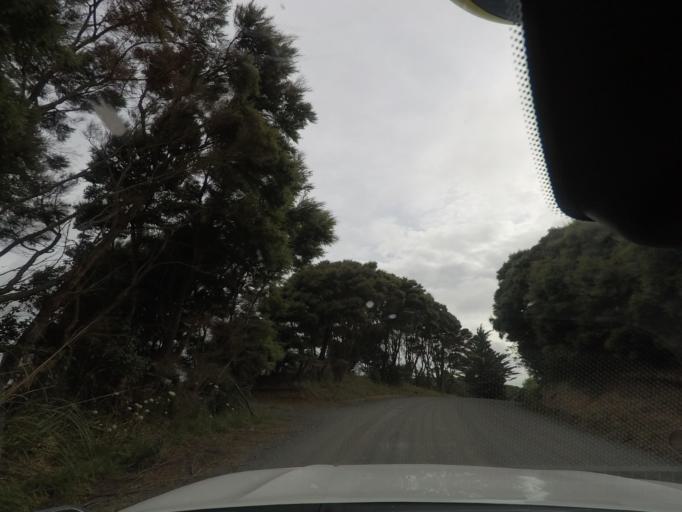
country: NZ
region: Auckland
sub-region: Auckland
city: Parakai
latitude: -36.4858
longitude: 174.2475
